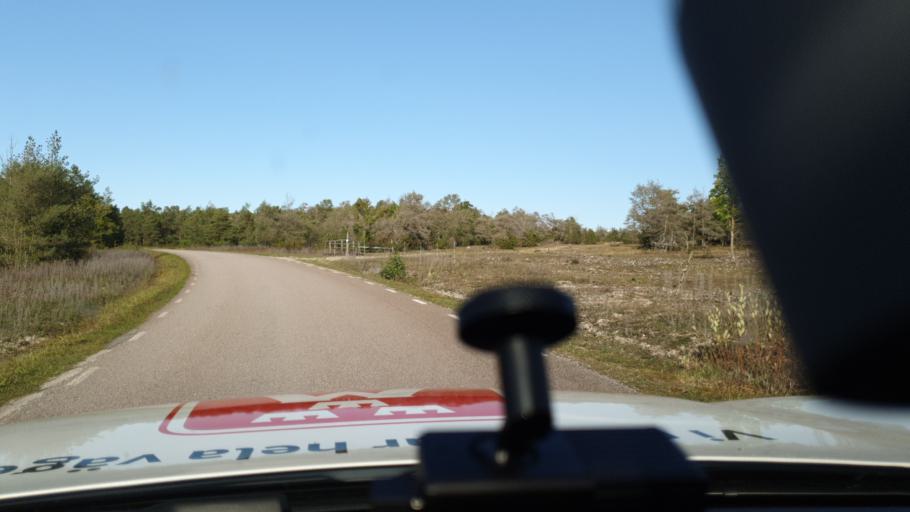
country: SE
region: Gotland
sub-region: Gotland
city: Slite
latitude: 57.6818
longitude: 18.6394
